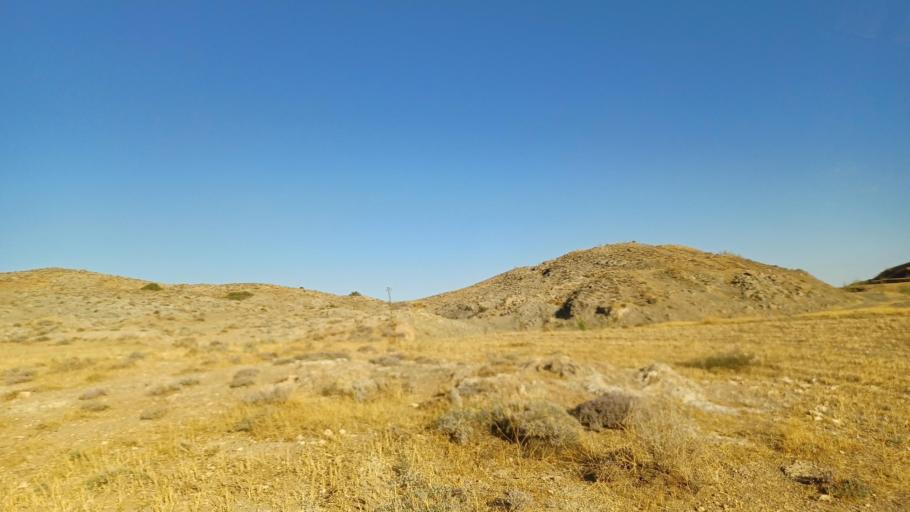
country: CY
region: Larnaka
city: Voroklini
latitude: 35.0048
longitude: 33.6379
